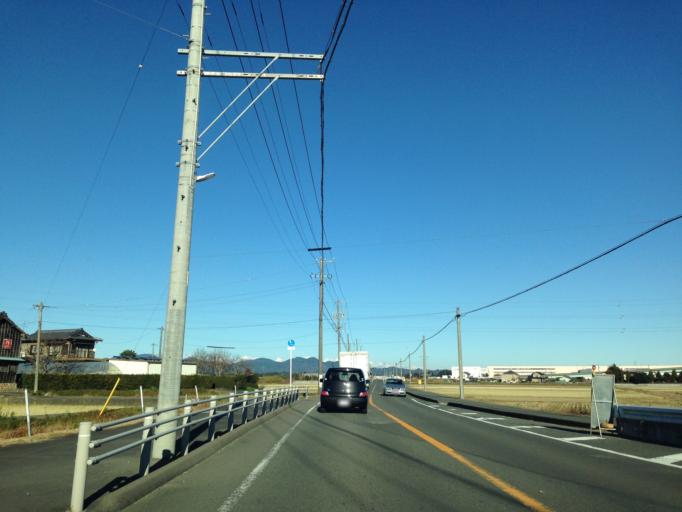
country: JP
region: Shizuoka
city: Fukuroi
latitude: 34.7557
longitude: 137.9666
